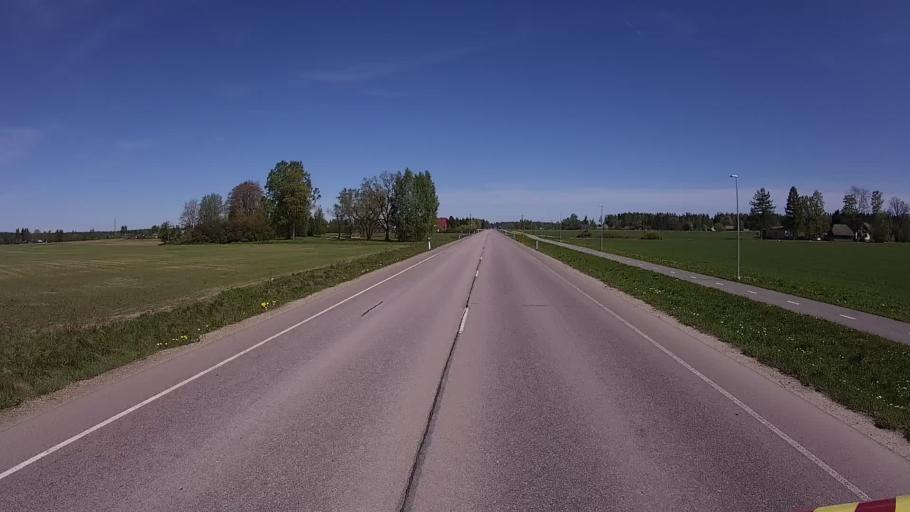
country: EE
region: Polvamaa
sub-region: Polva linn
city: Polva
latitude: 58.0782
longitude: 27.0892
